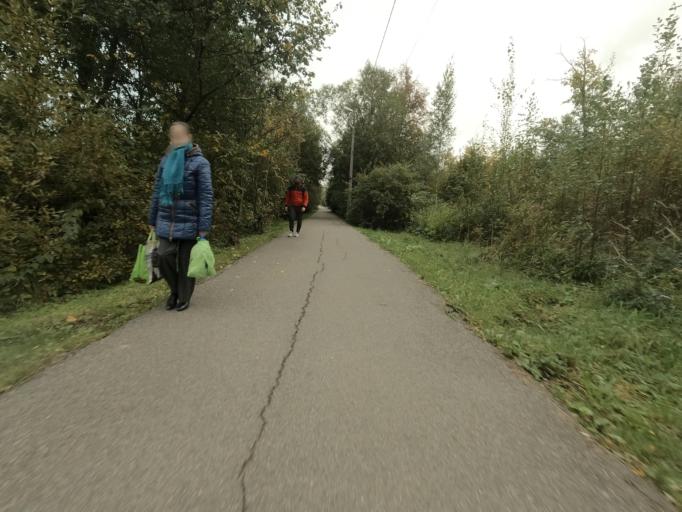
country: RU
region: St.-Petersburg
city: Pontonnyy
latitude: 59.7878
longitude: 30.6182
